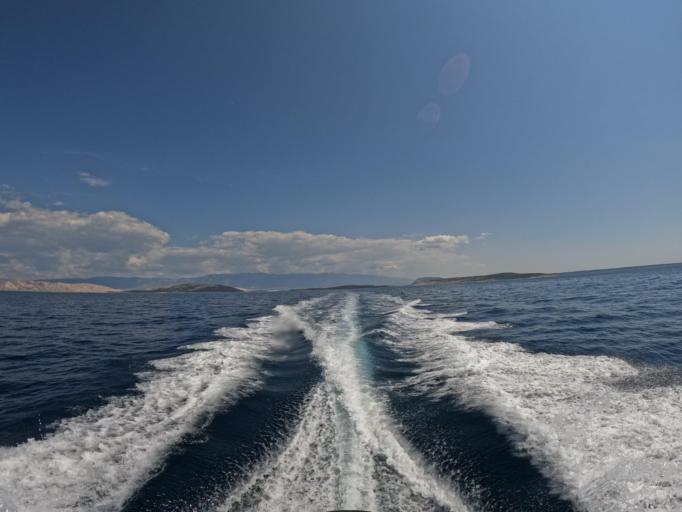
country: HR
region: Primorsko-Goranska
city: Lopar
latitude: 44.8739
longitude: 14.6662
